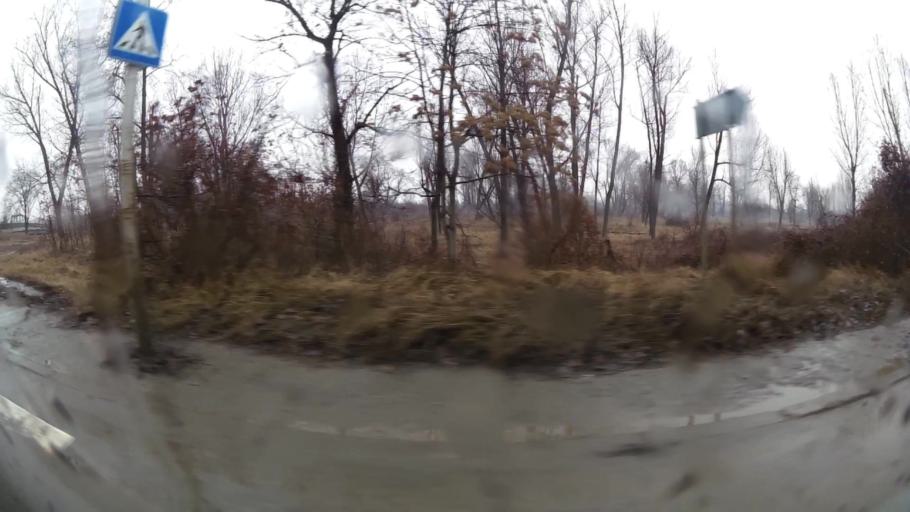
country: BG
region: Sofia-Capital
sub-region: Stolichna Obshtina
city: Sofia
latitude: 42.6655
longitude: 23.4222
